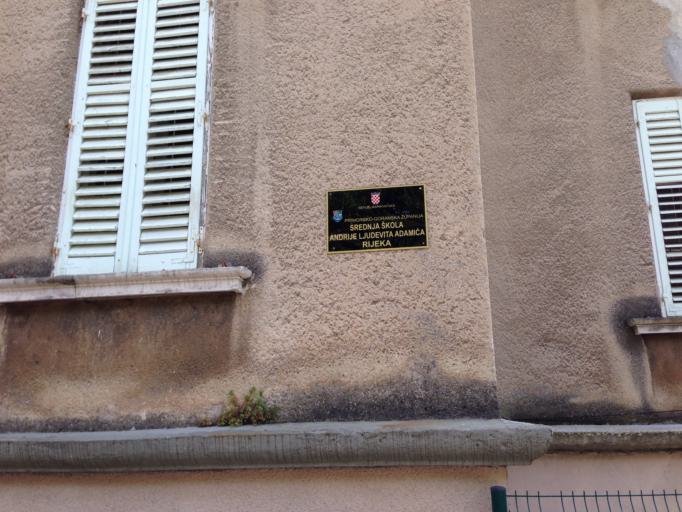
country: HR
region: Primorsko-Goranska
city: Cavle
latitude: 45.3163
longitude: 14.4686
